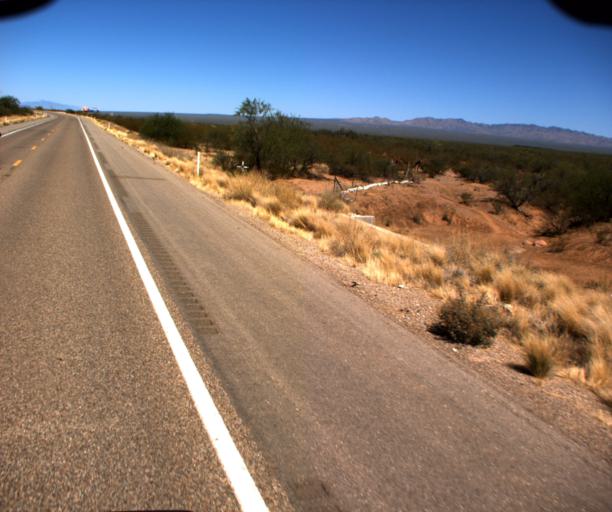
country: US
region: Arizona
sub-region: Pima County
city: Three Points
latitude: 32.0414
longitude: -111.4480
